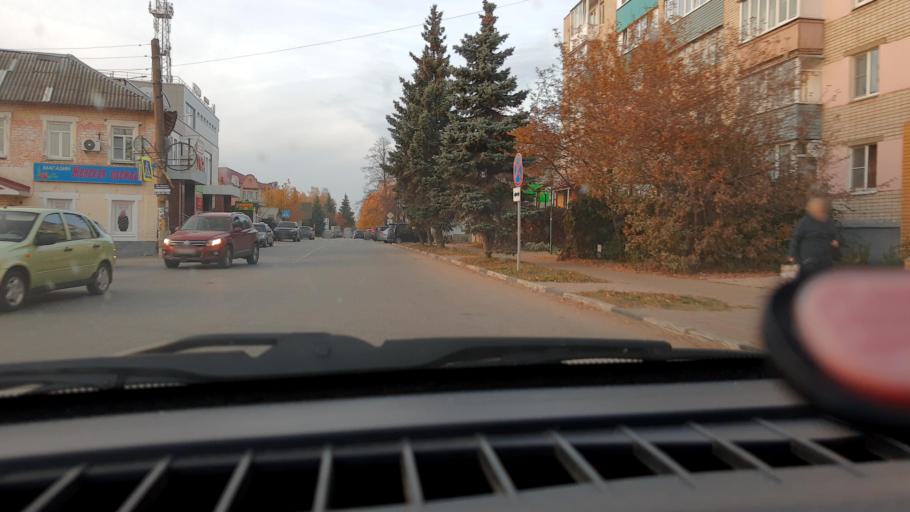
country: RU
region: Nizjnij Novgorod
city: Gorodets
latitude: 56.6457
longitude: 43.4723
